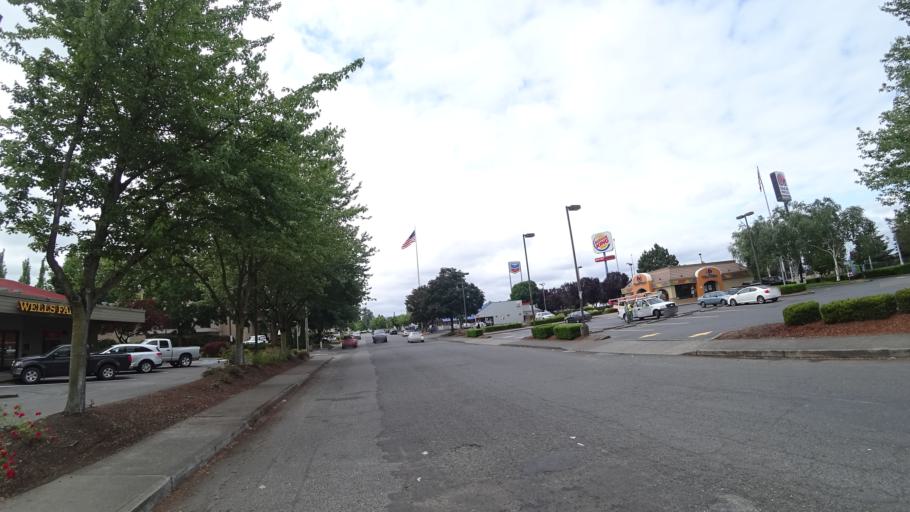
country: US
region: Washington
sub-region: Clark County
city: Vancouver
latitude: 45.6118
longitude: -122.6761
